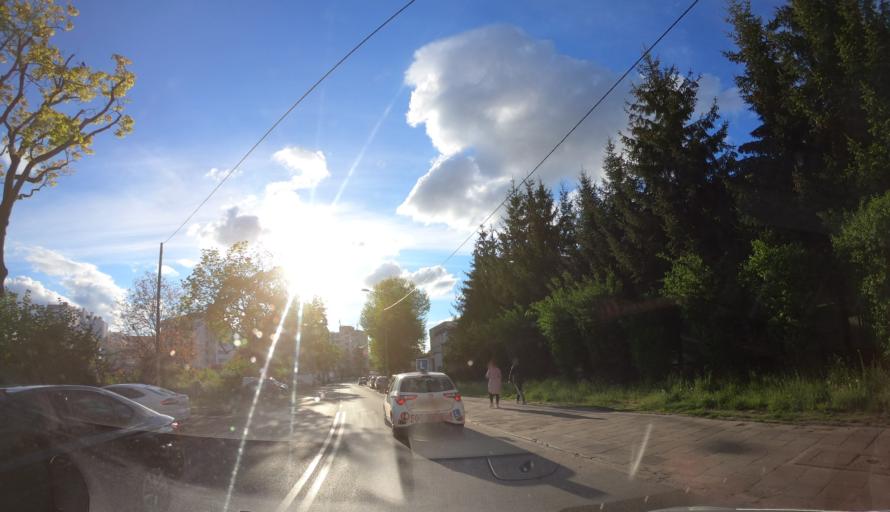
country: PL
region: West Pomeranian Voivodeship
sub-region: Szczecin
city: Szczecin
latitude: 53.4157
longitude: 14.5360
